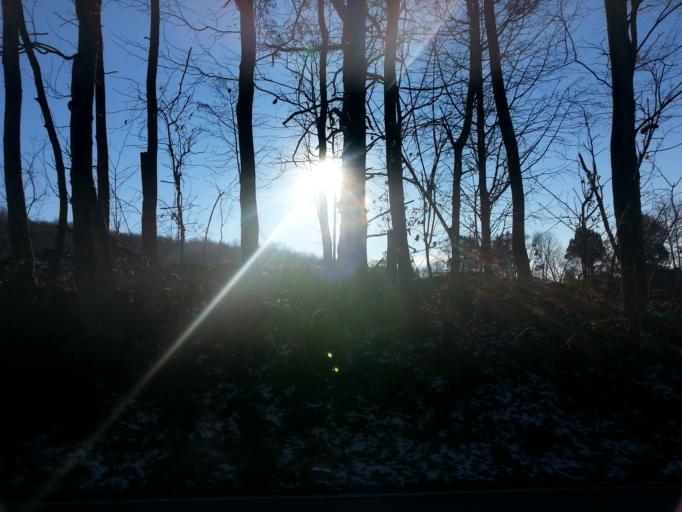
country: US
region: Tennessee
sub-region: Knox County
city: Farragut
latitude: 35.9669
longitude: -84.0802
